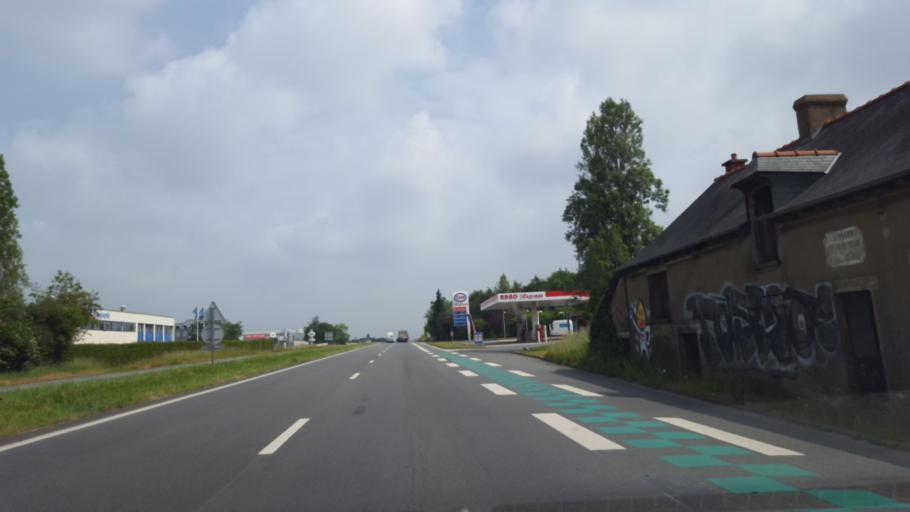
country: FR
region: Brittany
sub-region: Departement d'Ille-et-Vilaine
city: Saint-Jacques-de-la-Lande
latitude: 48.0641
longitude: -1.6989
